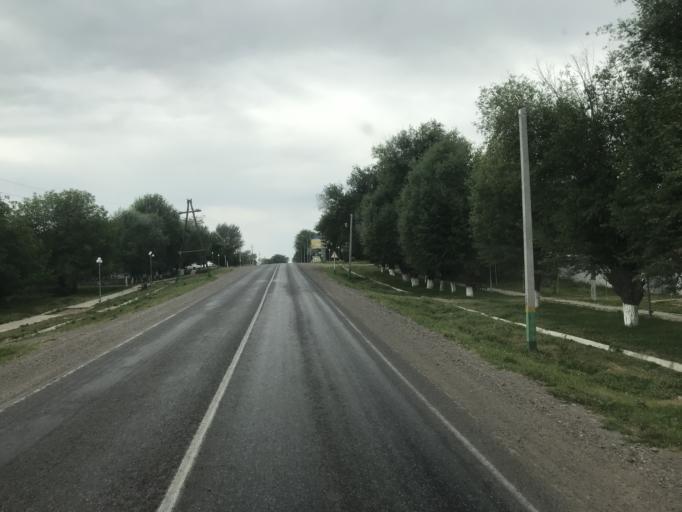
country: UZ
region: Toshkent
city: Salor
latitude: 41.4937
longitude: 69.3055
